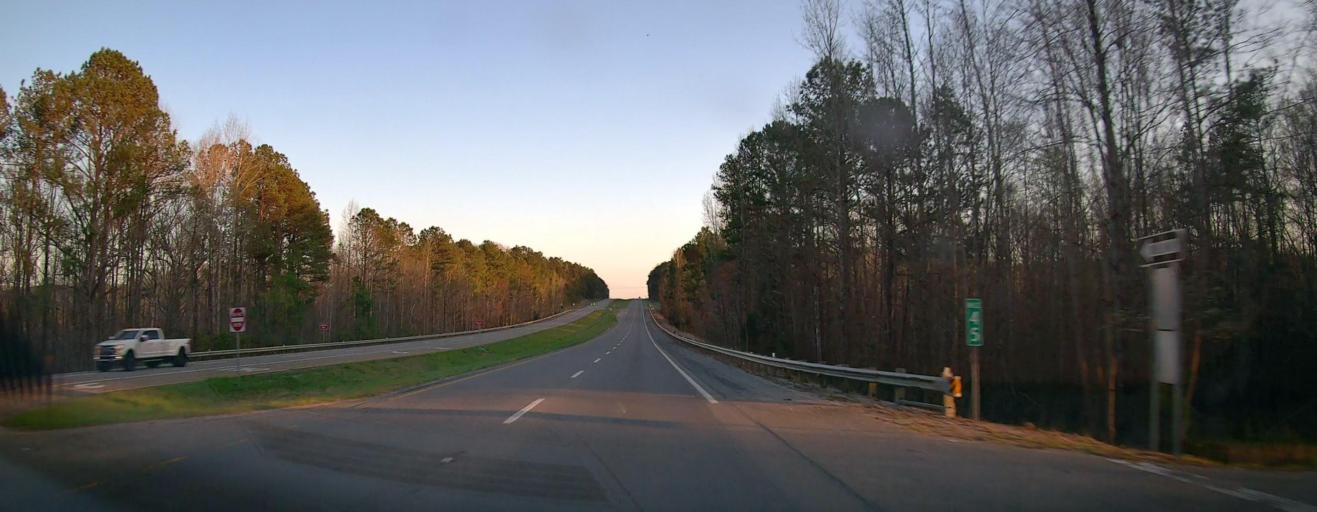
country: US
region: Alabama
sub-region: Talladega County
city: Sylacauga
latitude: 33.1324
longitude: -86.2467
